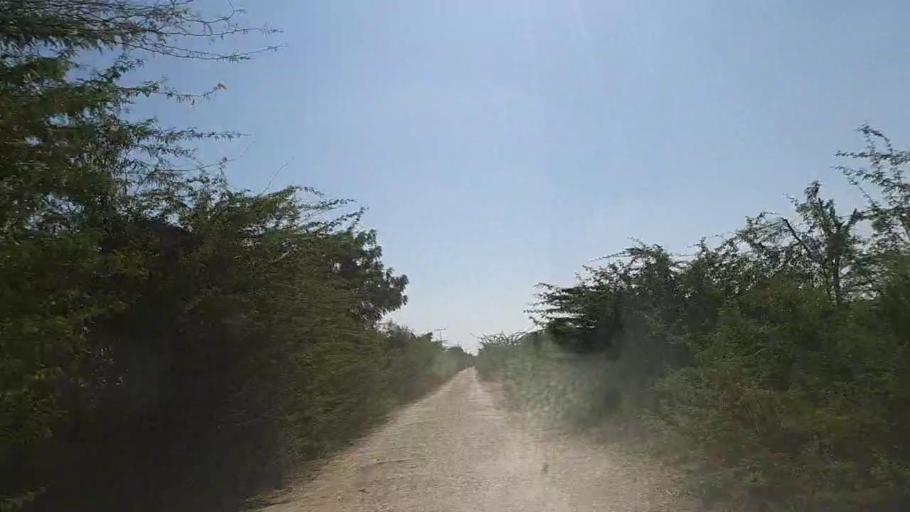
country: PK
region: Sindh
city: Naukot
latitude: 25.0001
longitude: 69.3724
